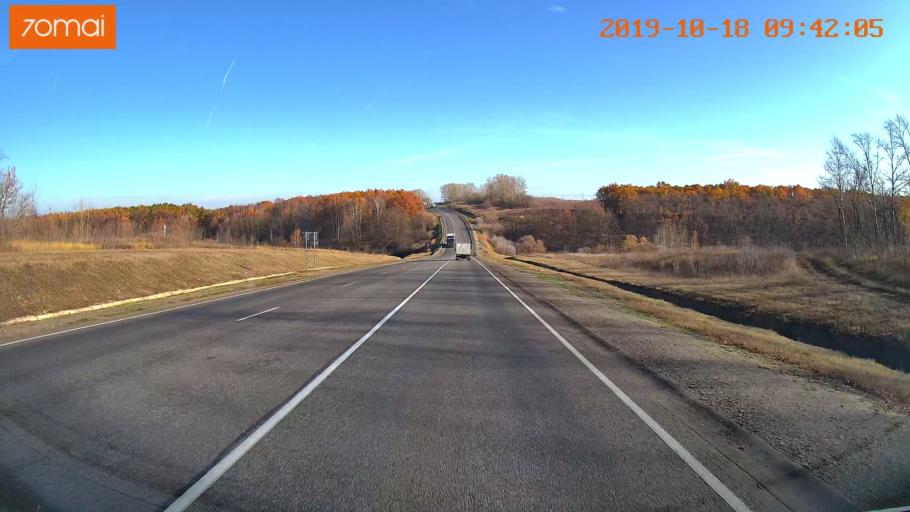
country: RU
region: Tula
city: Kazachka
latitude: 53.2827
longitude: 38.1715
